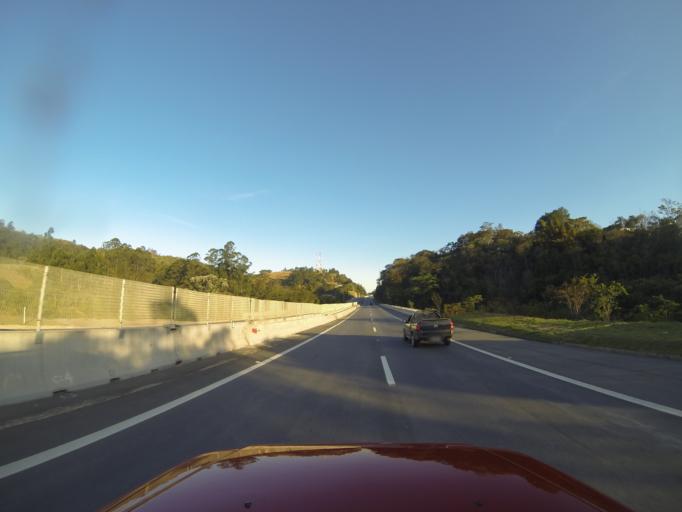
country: BR
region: Sao Paulo
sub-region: Santa Branca
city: Santa Branca
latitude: -23.3775
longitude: -45.6647
